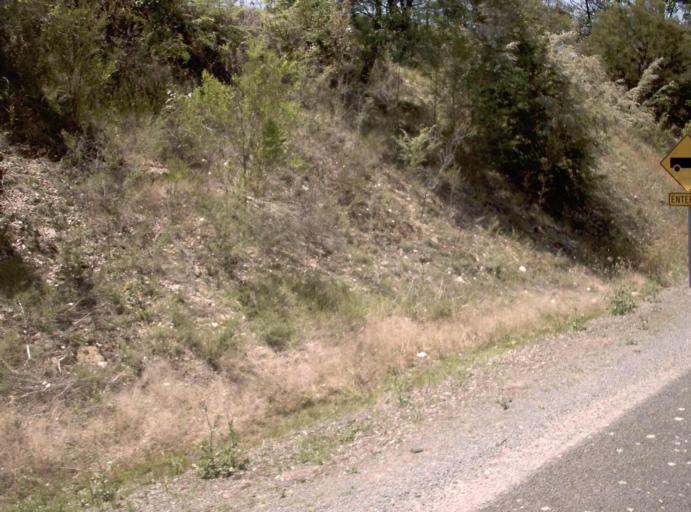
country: AU
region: Victoria
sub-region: East Gippsland
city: Lakes Entrance
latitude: -37.7027
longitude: 148.5571
